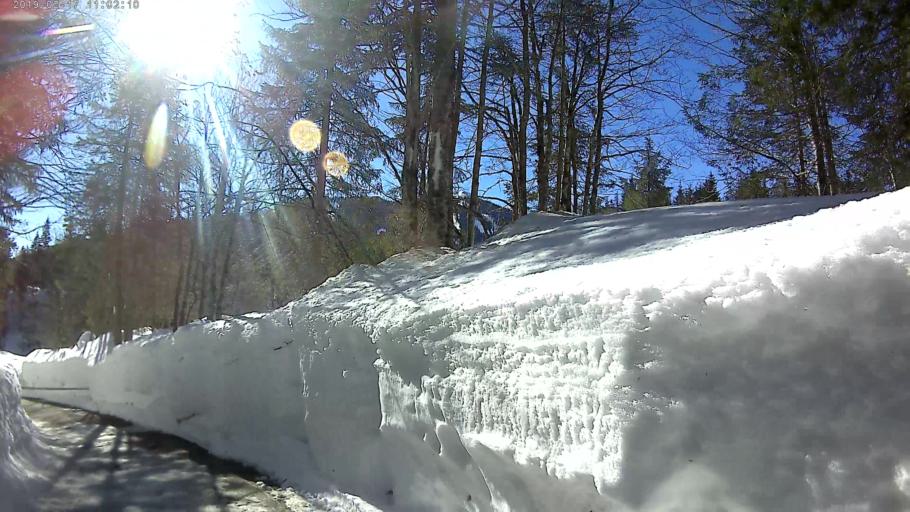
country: AT
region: Salzburg
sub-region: Politischer Bezirk Sankt Johann im Pongau
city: Muhlbach am Hochkonig
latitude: 47.3950
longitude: 13.0804
